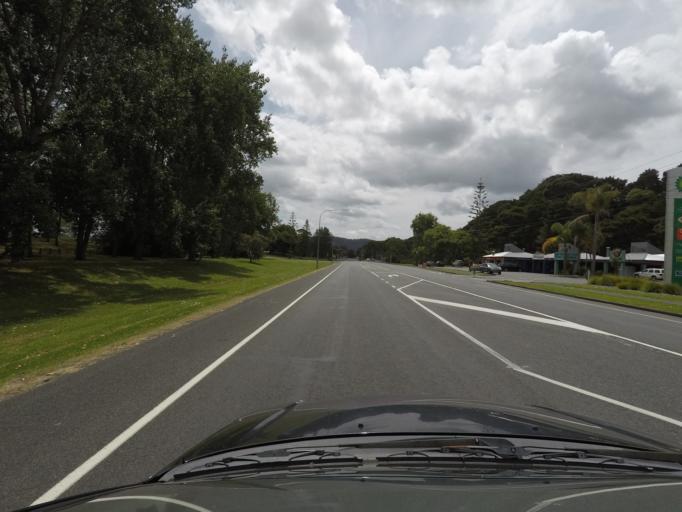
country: NZ
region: Northland
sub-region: Whangarei
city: Whangarei
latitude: -35.7293
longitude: 174.3385
